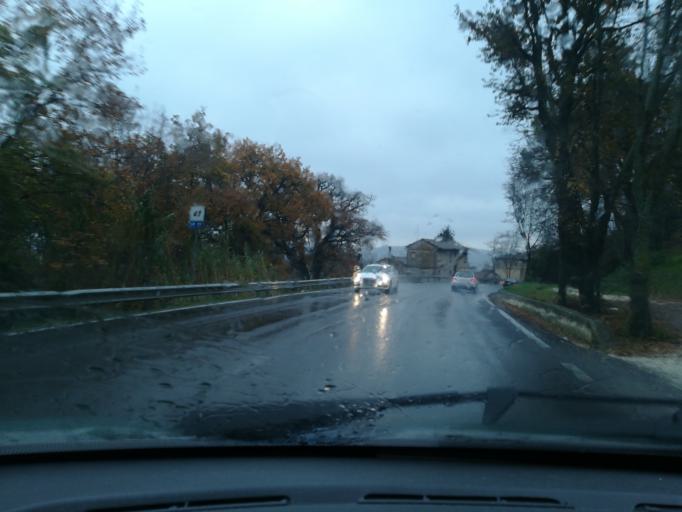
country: IT
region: The Marches
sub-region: Provincia di Macerata
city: Sforzacosta
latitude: 43.2797
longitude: 13.4323
